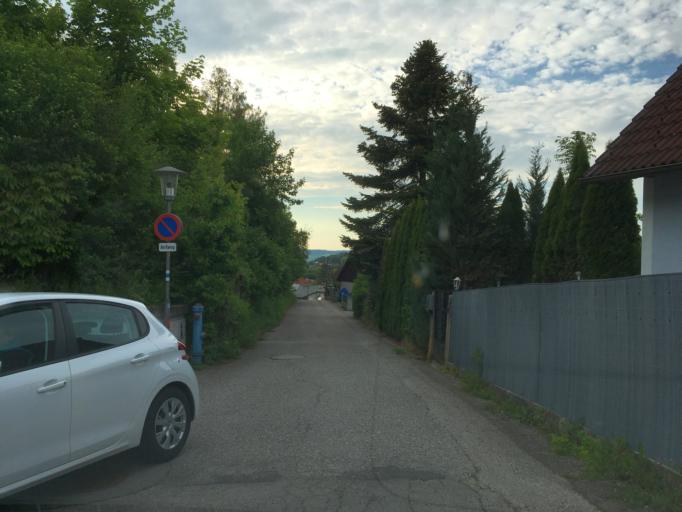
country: AT
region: Lower Austria
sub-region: Politischer Bezirk Sankt Polten
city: Maria-Anzbach
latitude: 48.1883
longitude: 15.9342
